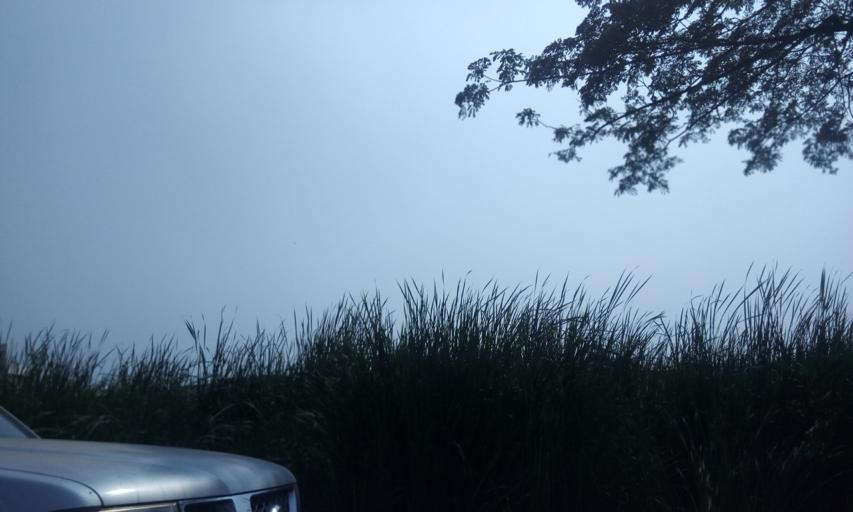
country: TH
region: Pathum Thani
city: Lam Luk Ka
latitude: 13.9646
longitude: 100.7375
